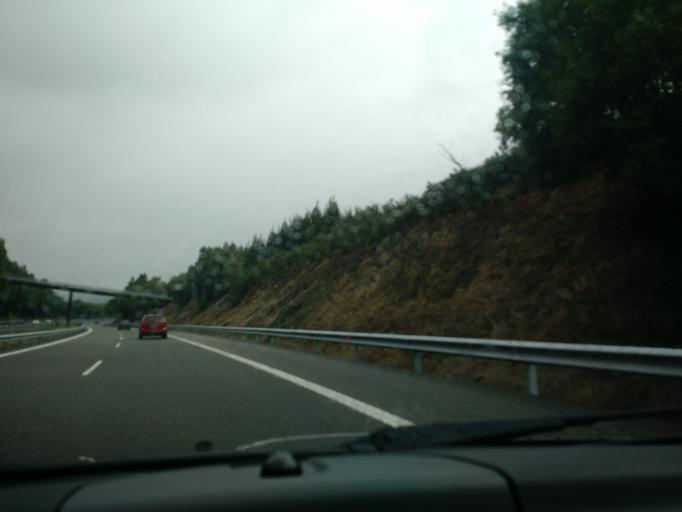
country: ES
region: Galicia
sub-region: Provincia da Coruna
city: Mesia
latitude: 43.1274
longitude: -8.3282
